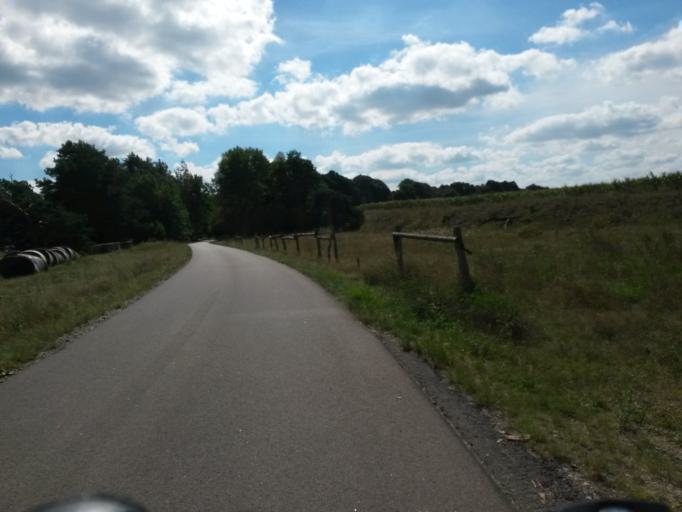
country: DE
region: Brandenburg
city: Templin
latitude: 53.1552
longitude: 13.5282
